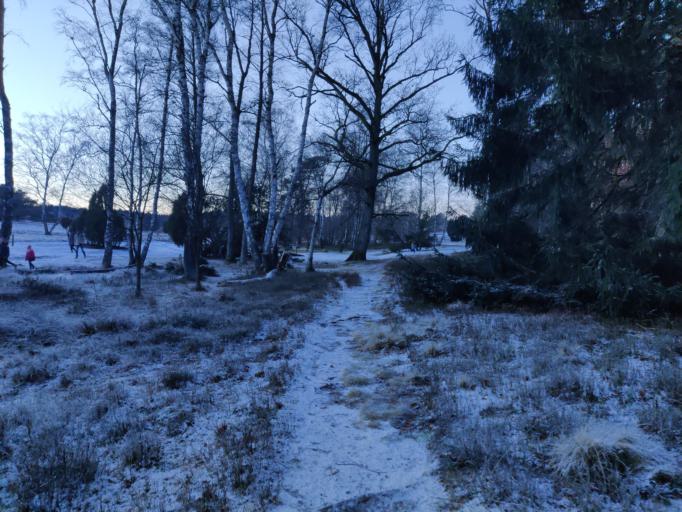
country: DE
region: Lower Saxony
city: Handeloh
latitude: 53.2722
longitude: 9.8473
